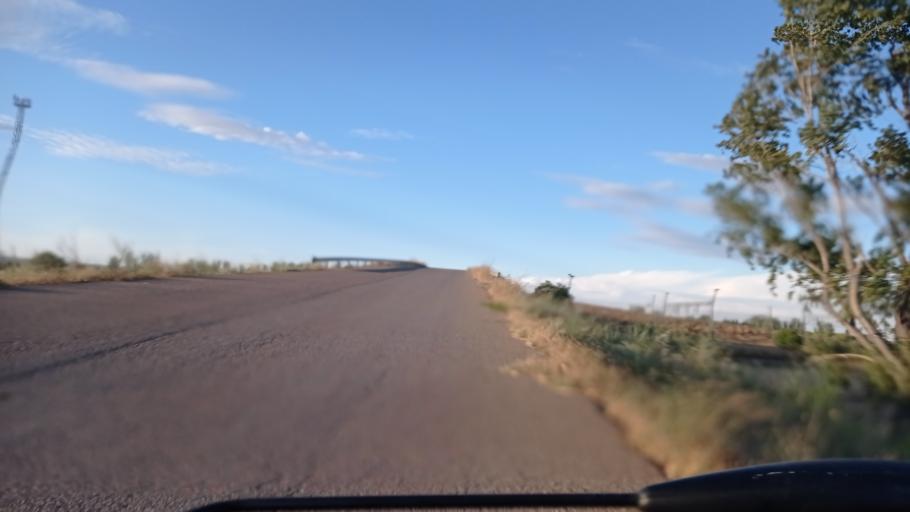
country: ES
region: Aragon
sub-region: Provincia de Zaragoza
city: Oliver-Valdefierro, Oliver, Valdefierro
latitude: 41.6744
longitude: -0.9412
